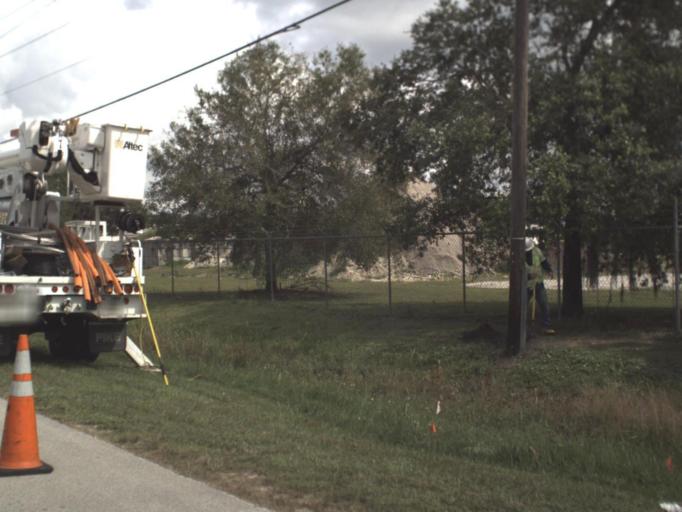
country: US
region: Florida
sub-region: Hendry County
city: LaBelle
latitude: 26.7449
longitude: -81.4379
